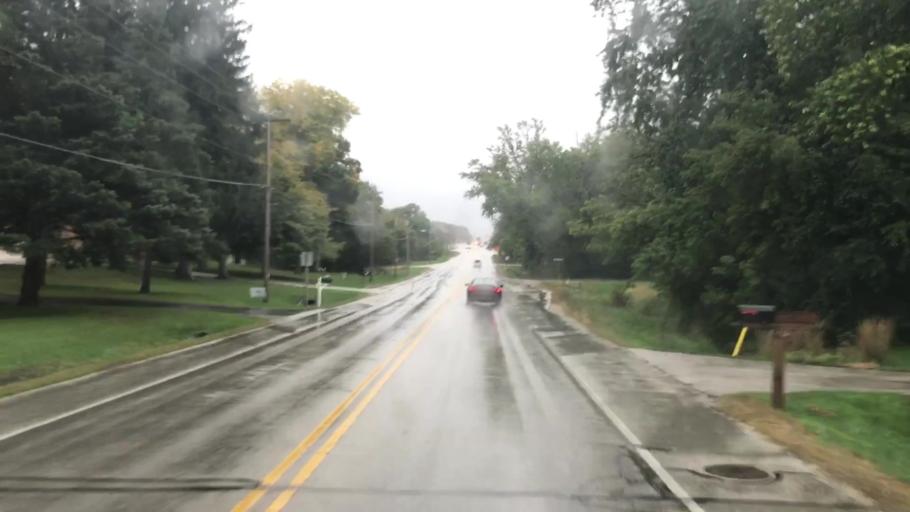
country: US
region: Wisconsin
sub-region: Ozaukee County
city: Mequon
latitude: 43.2275
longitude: -88.0036
